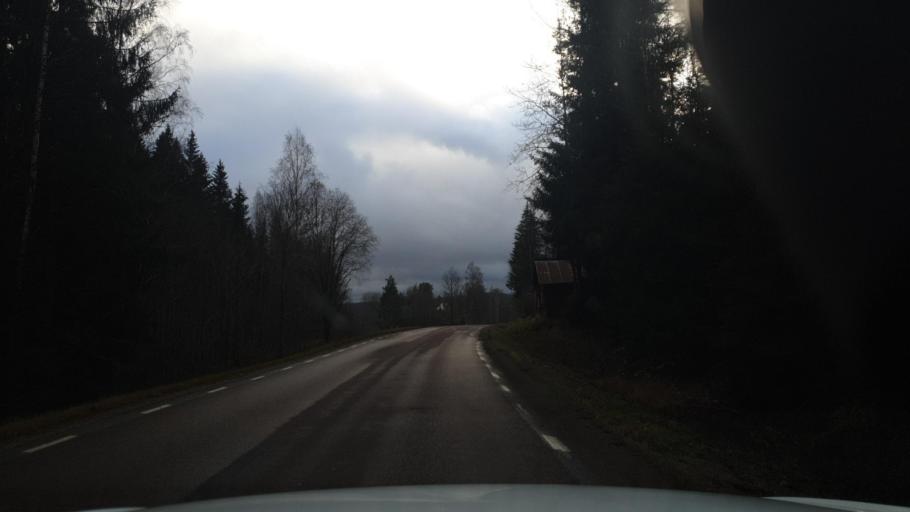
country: SE
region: Vaermland
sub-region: Arvika Kommun
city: Arvika
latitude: 59.6916
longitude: 12.7913
